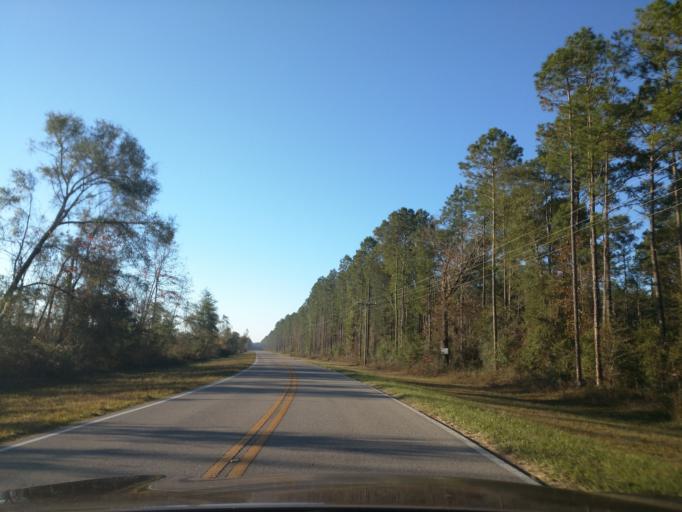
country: US
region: Florida
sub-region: Leon County
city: Woodville
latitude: 30.3434
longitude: -84.1414
